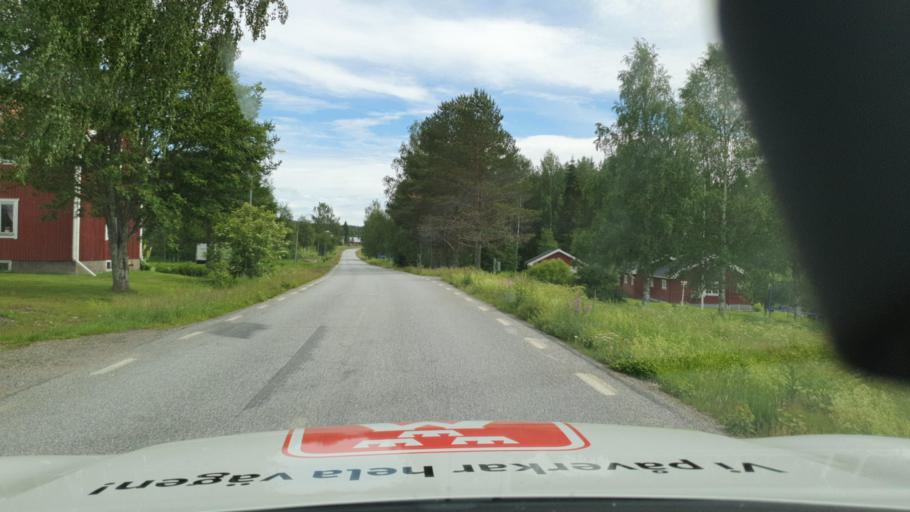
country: SE
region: Vaesterbotten
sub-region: Skelleftea Kommun
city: Soedra Bergsbyn
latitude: 64.5092
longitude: 21.0022
